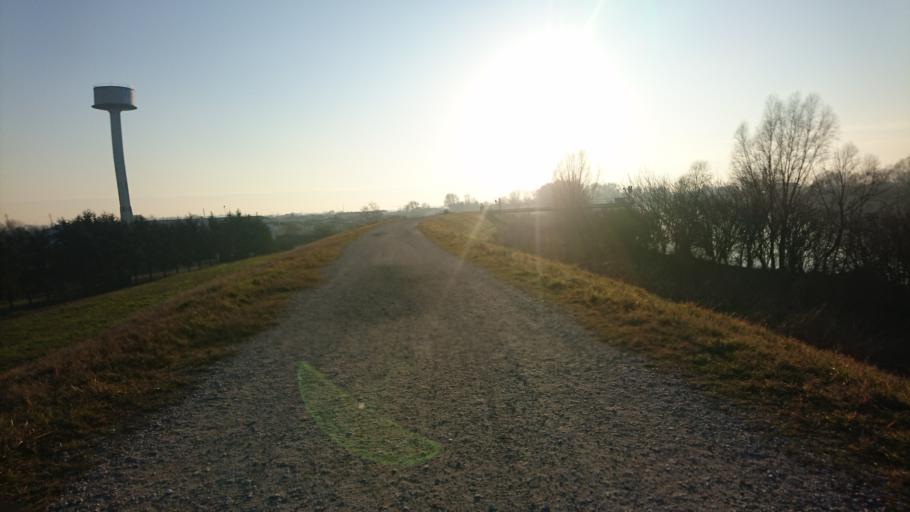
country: IT
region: Veneto
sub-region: Provincia di Padova
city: Boara Pisani
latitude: 45.1126
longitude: 11.7991
